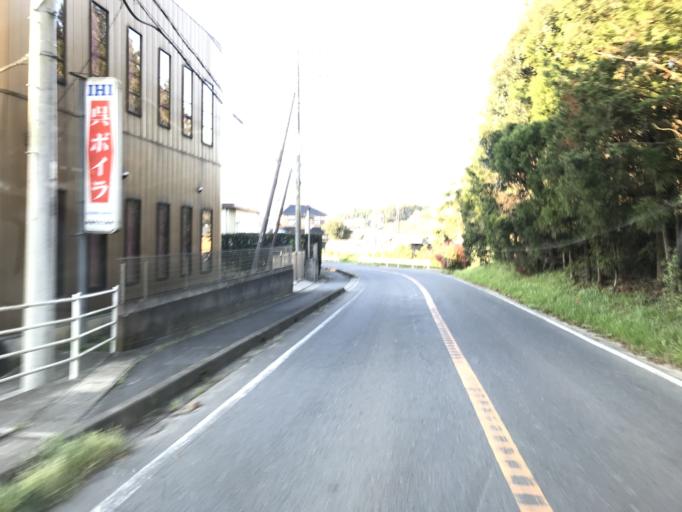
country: JP
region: Chiba
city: Yokaichiba
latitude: 35.7413
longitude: 140.5569
